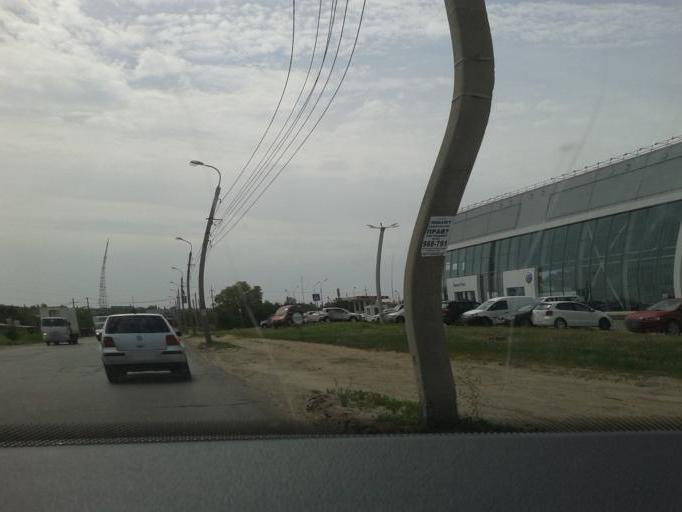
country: RU
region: Volgograd
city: Volgograd
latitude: 48.7570
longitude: 44.5235
